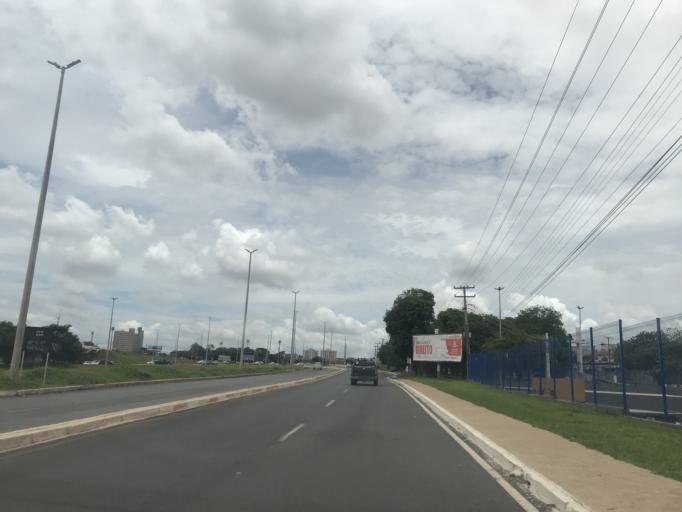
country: BR
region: Federal District
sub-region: Brasilia
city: Brasilia
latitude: -15.8346
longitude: -48.0745
